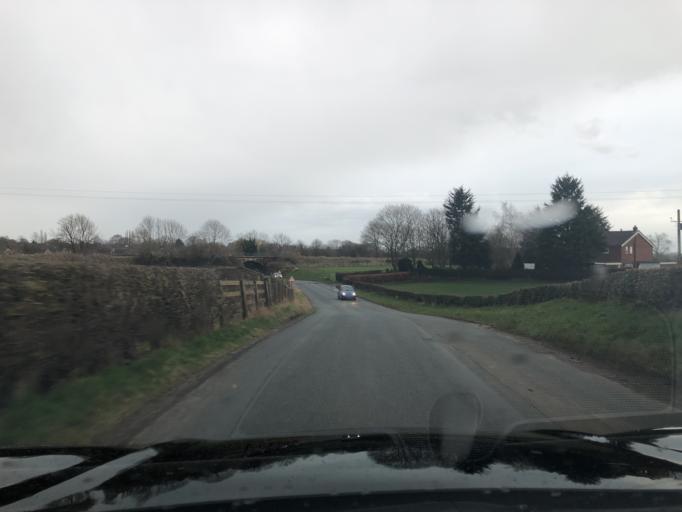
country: GB
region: England
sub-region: North Yorkshire
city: Northallerton
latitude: 54.3398
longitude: -1.4524
